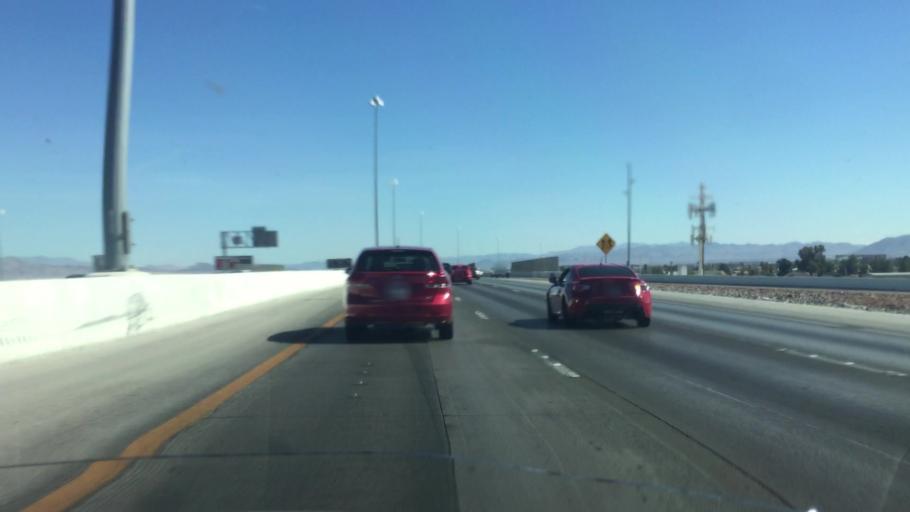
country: US
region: Nevada
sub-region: Clark County
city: Spring Valley
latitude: 36.0681
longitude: -115.2054
